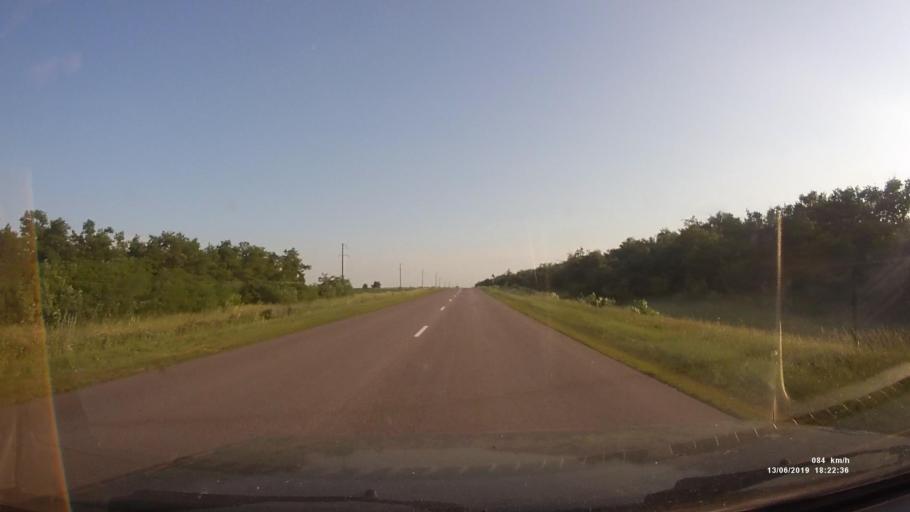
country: RU
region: Rostov
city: Kazanskaya
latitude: 49.8566
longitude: 41.2771
